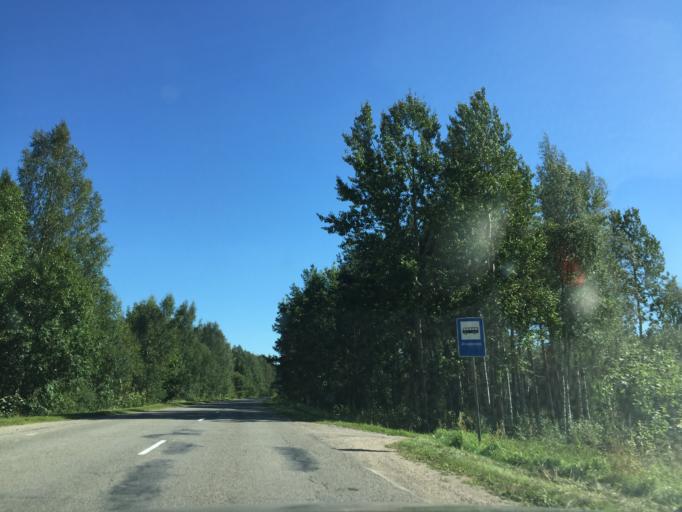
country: LV
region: Akniste
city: Akniste
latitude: 56.1385
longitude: 25.8163
